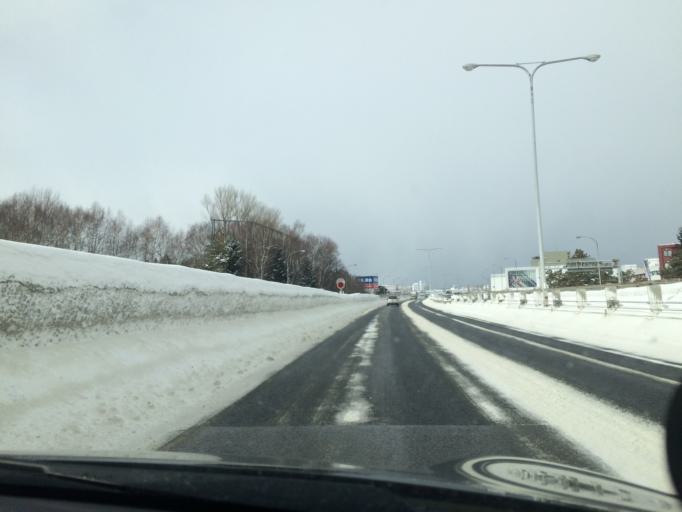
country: JP
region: Hokkaido
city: Sapporo
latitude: 43.0255
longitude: 141.4513
